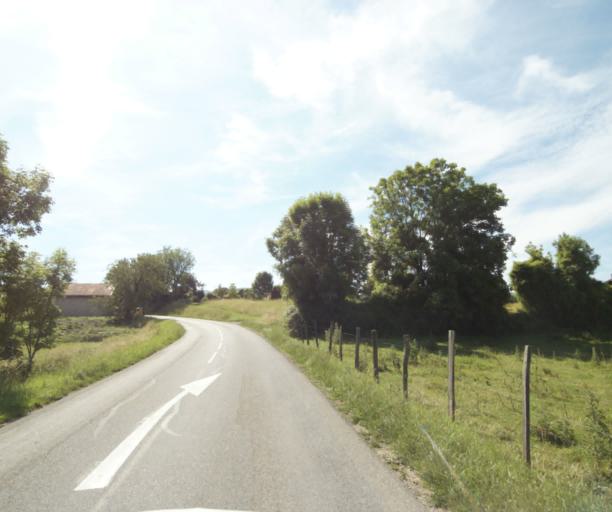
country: FR
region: Rhone-Alpes
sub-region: Departement de la Haute-Savoie
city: Margencel
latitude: 46.3312
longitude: 6.4190
